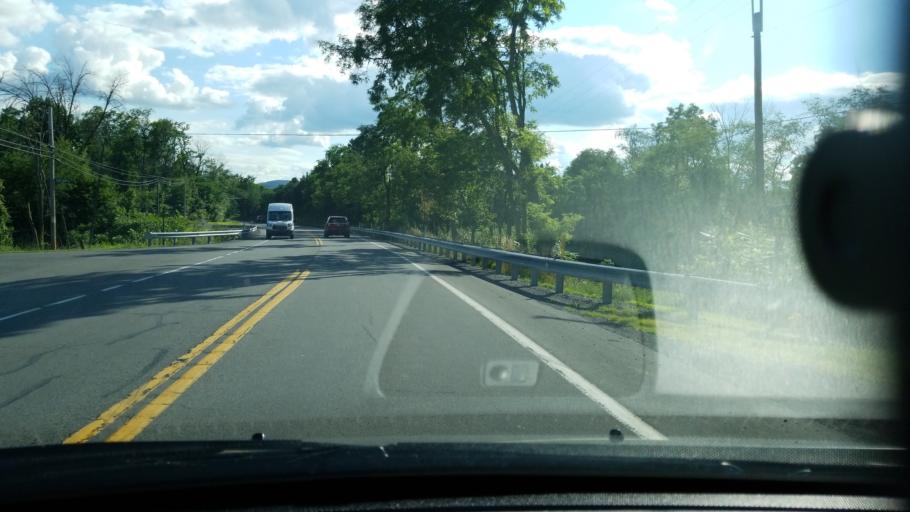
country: US
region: Pennsylvania
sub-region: Northumberland County
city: Elysburg
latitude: 40.8710
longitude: -76.5409
